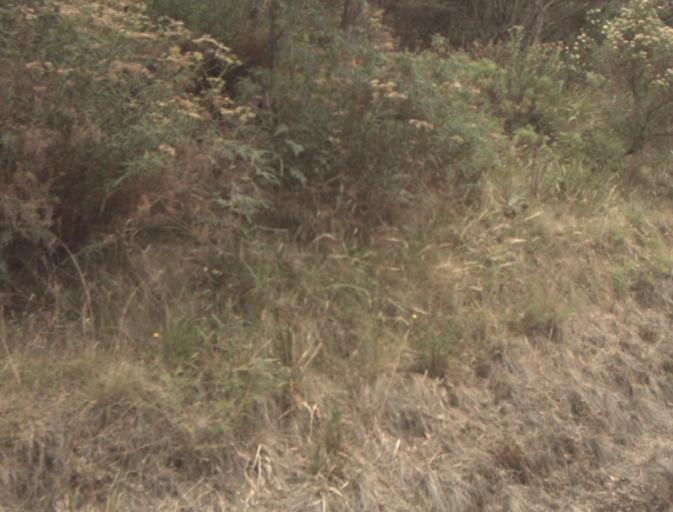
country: AU
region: Tasmania
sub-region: Northern Midlands
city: Evandale
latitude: -41.5200
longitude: 147.4071
